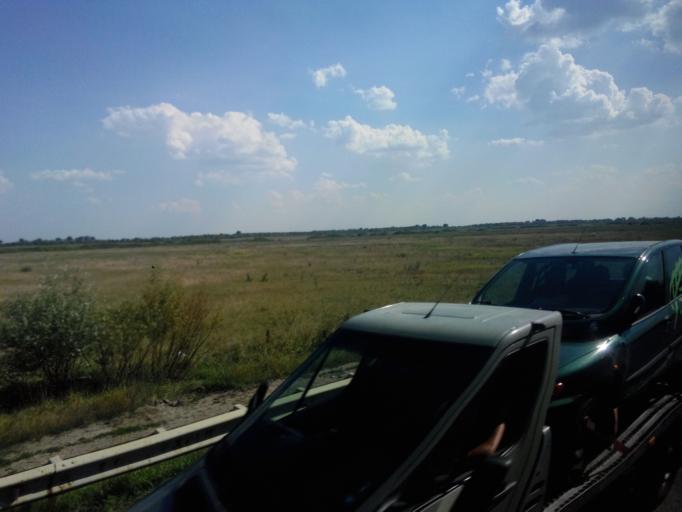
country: RO
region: Timis
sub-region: Comuna Remetea Mare
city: Remetea Mare
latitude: 45.7889
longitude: 21.4011
